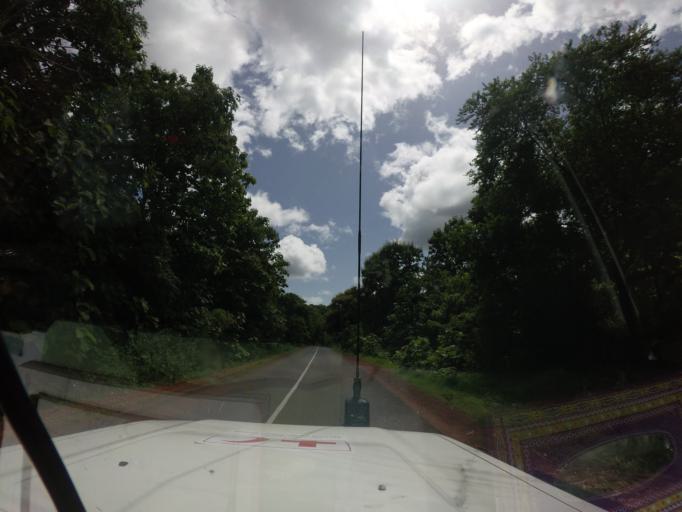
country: SL
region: Northern Province
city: Bindi
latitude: 10.1735
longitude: -11.7151
